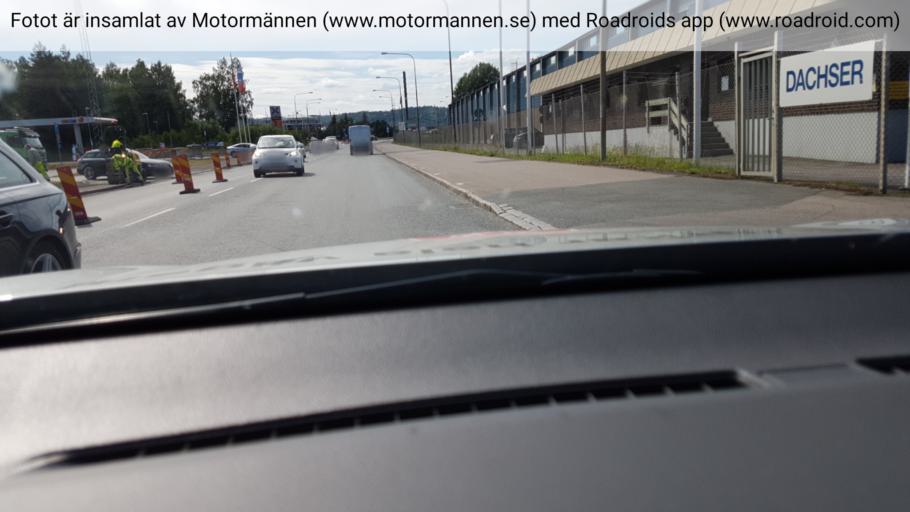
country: SE
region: Joenkoeping
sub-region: Jonkopings Kommun
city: Jonkoping
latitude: 57.7616
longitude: 14.1715
